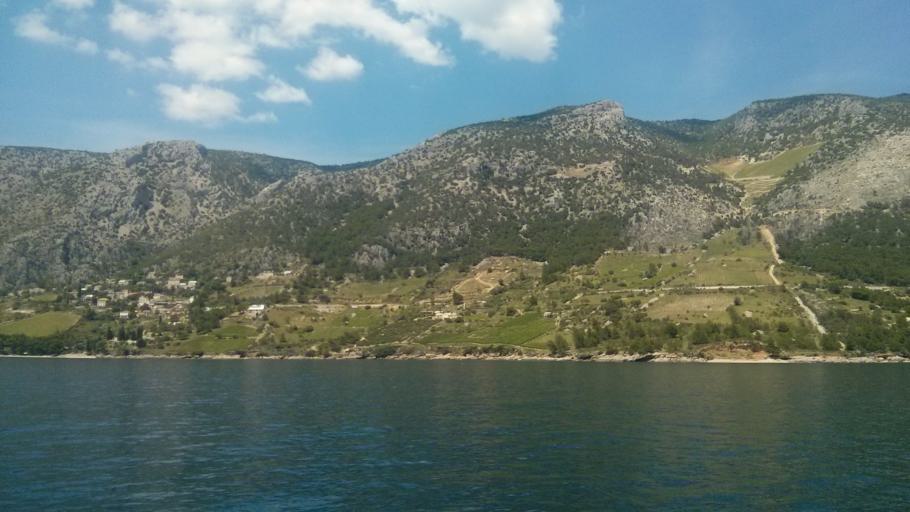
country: HR
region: Splitsko-Dalmatinska
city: Bol
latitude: 43.2574
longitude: 16.5985
